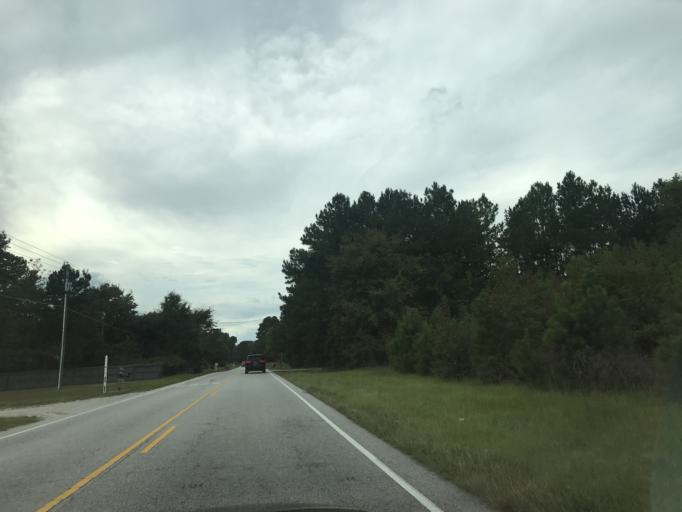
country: US
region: North Carolina
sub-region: Franklin County
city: Youngsville
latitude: 35.9978
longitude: -78.4190
